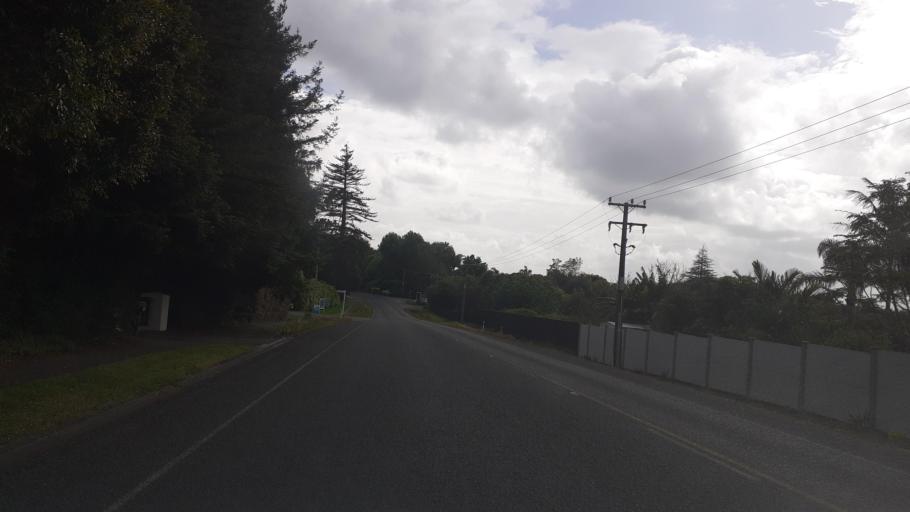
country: NZ
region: Northland
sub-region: Far North District
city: Kerikeri
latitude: -35.2222
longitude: 173.9760
